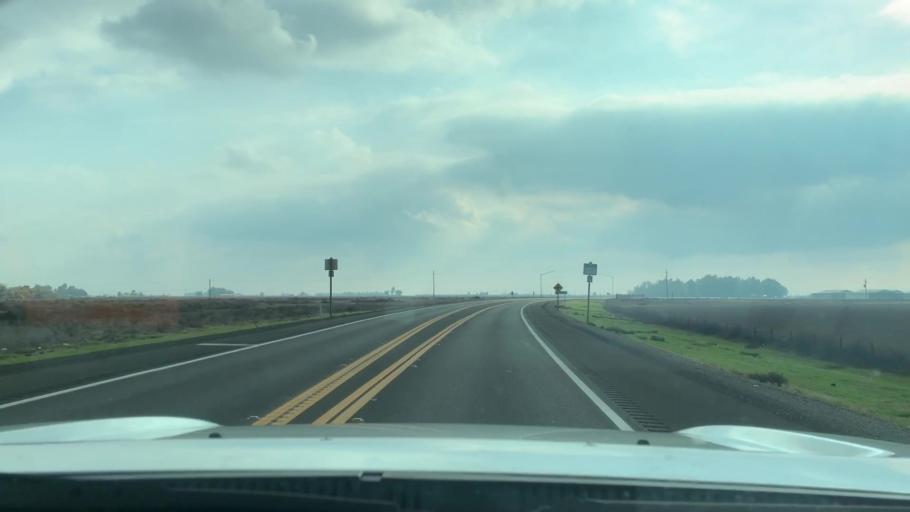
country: US
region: California
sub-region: Kings County
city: Lemoore
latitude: 36.2580
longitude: -119.8079
